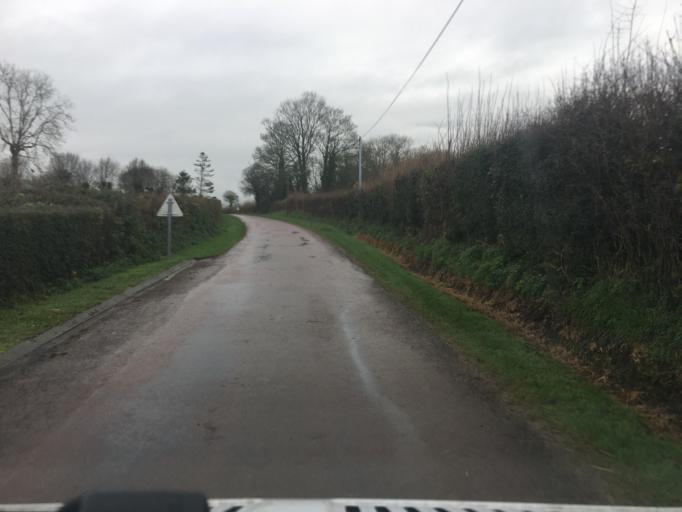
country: FR
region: Lower Normandy
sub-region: Departement de la Manche
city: Sainte-Mere-Eglise
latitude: 49.4283
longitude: -1.2633
